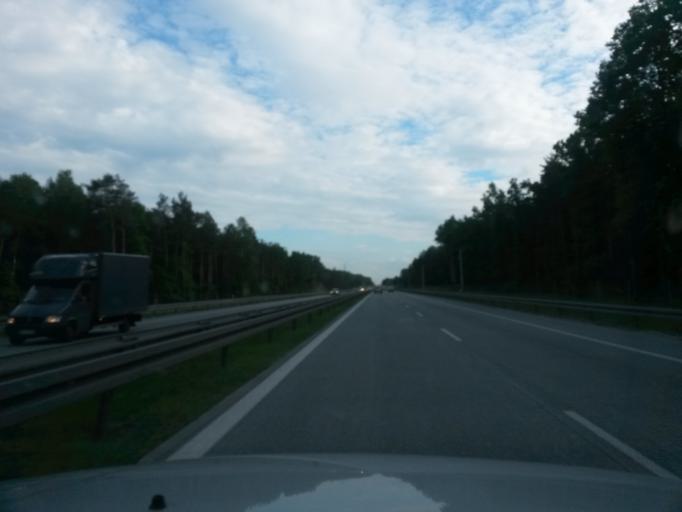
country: PL
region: Lodz Voivodeship
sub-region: Powiat tomaszowski
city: Lubochnia
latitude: 51.5749
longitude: 20.0276
